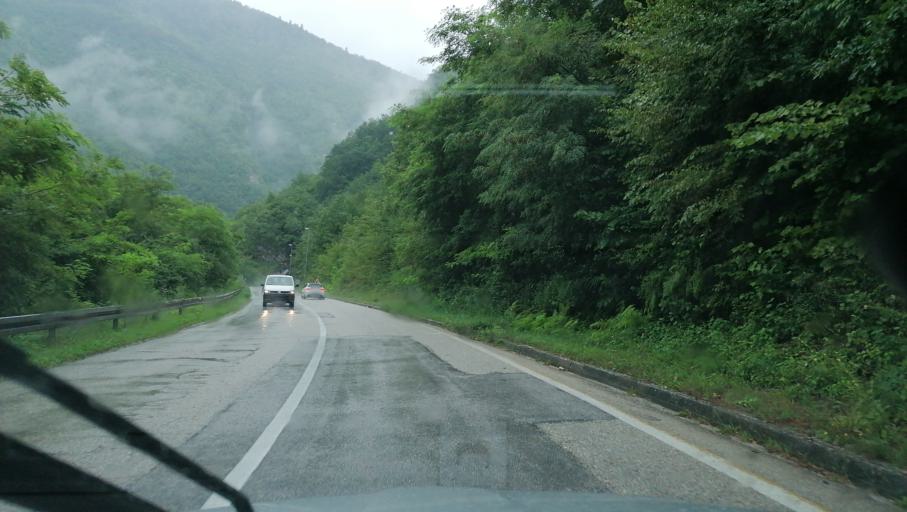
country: BA
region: Republika Srpska
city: Cajnice
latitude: 43.6830
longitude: 19.1497
